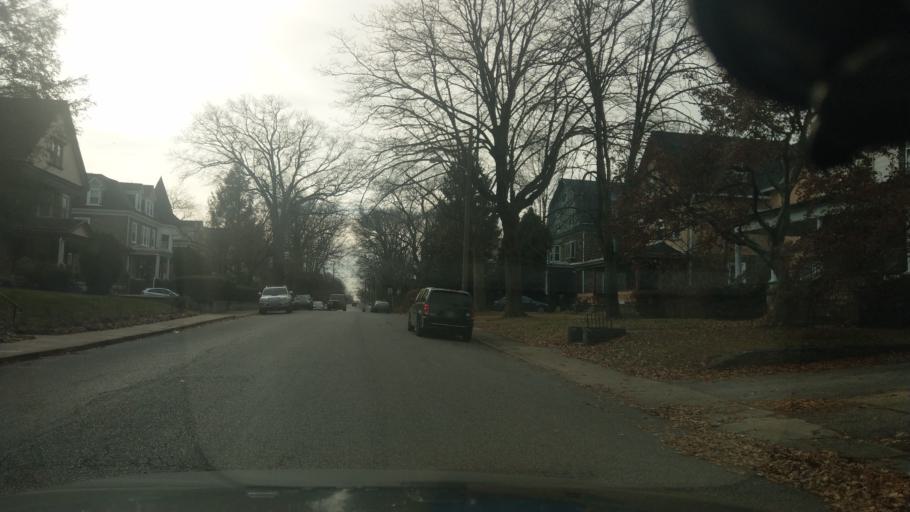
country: US
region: Pennsylvania
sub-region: Montgomery County
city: Wyncote
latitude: 40.0569
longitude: -75.1358
